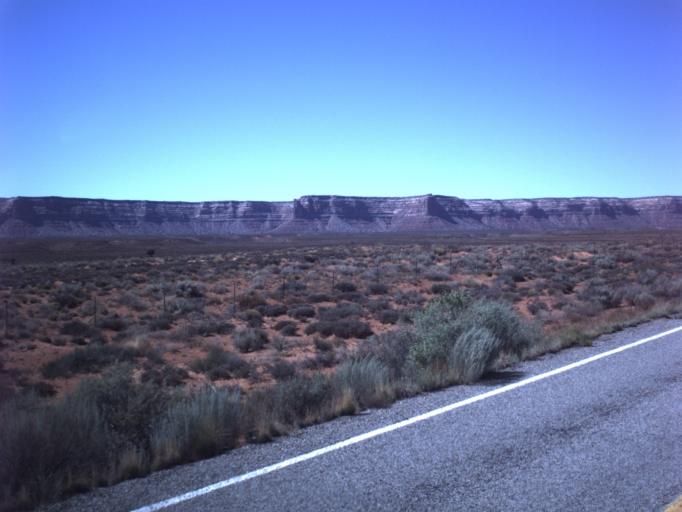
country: US
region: Utah
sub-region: San Juan County
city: Blanding
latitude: 37.2125
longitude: -109.8859
